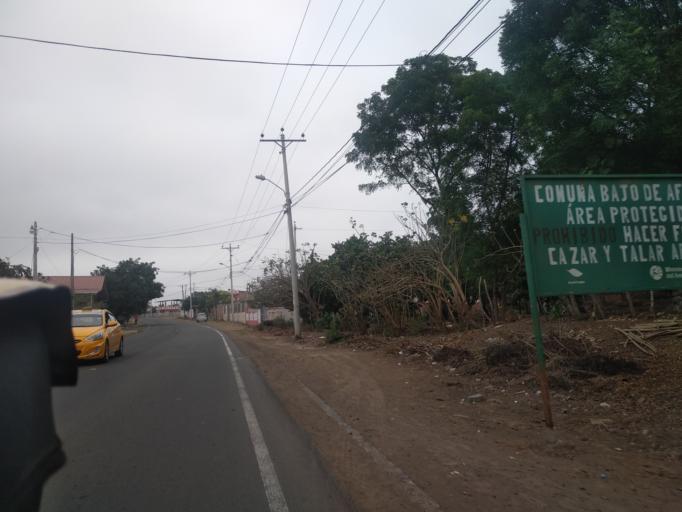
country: EC
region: Manabi
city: Montecristi
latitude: -1.0768
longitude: -80.6700
